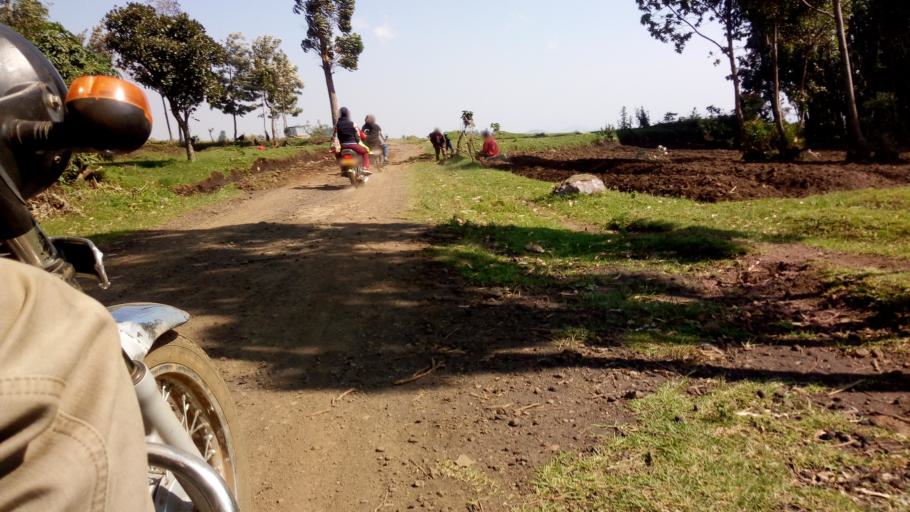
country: UG
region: Western Region
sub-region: Kisoro District
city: Kisoro
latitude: -1.3421
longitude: 29.6287
